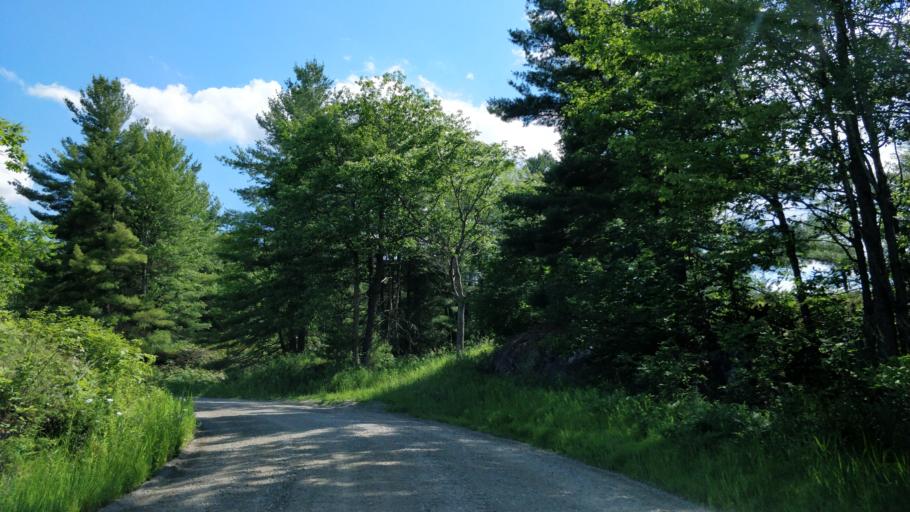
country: CA
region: Ontario
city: Perth
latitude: 44.6966
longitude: -76.5291
